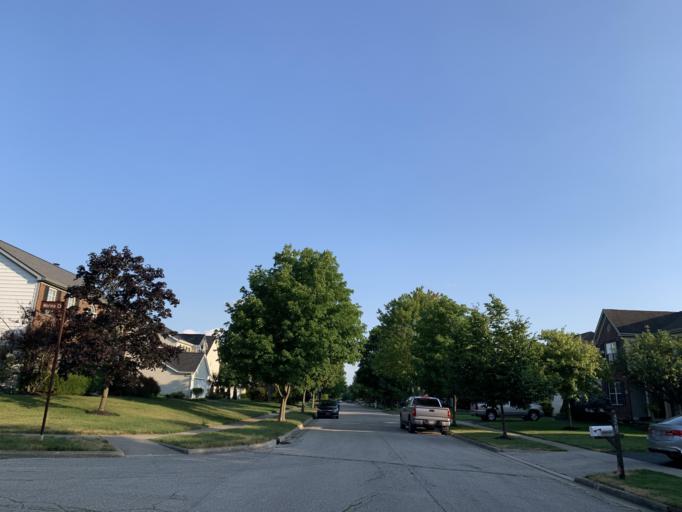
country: US
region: Ohio
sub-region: Franklin County
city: Dublin
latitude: 40.1178
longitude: -83.1707
